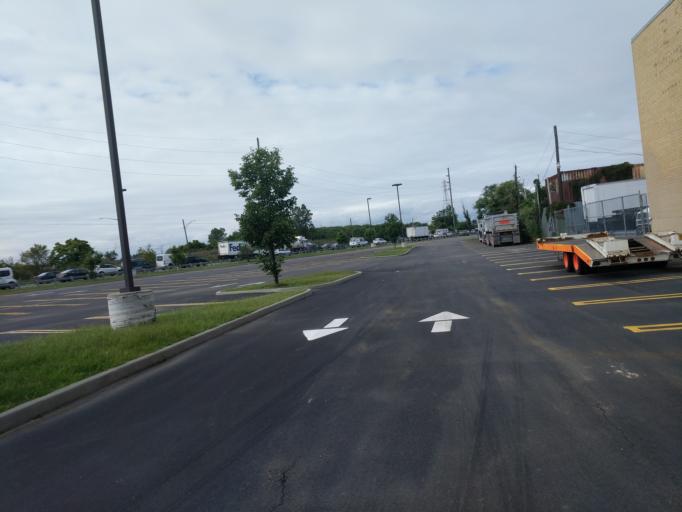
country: US
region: New York
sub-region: Nassau County
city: Inwood
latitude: 40.6249
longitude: -73.7401
